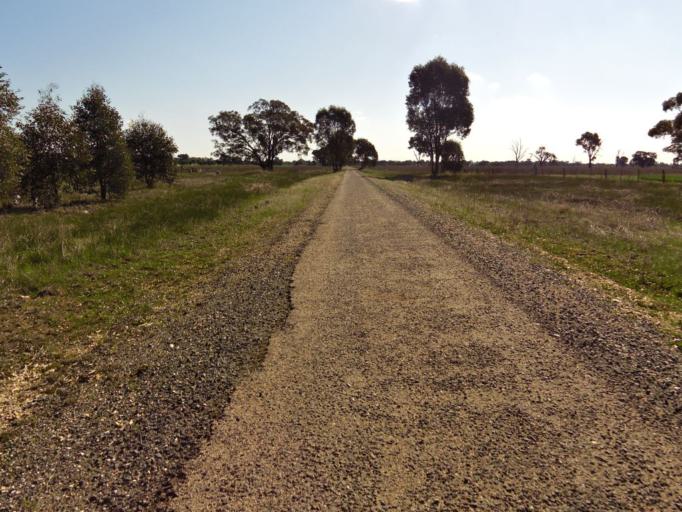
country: AU
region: New South Wales
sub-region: Corowa Shire
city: Corowa
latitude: -36.0208
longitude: 146.4228
